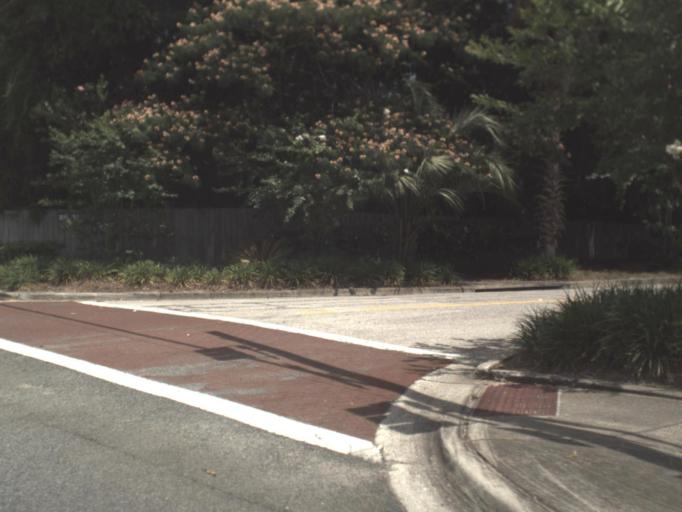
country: US
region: Florida
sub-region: Alachua County
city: Gainesville
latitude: 29.6135
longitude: -82.3552
